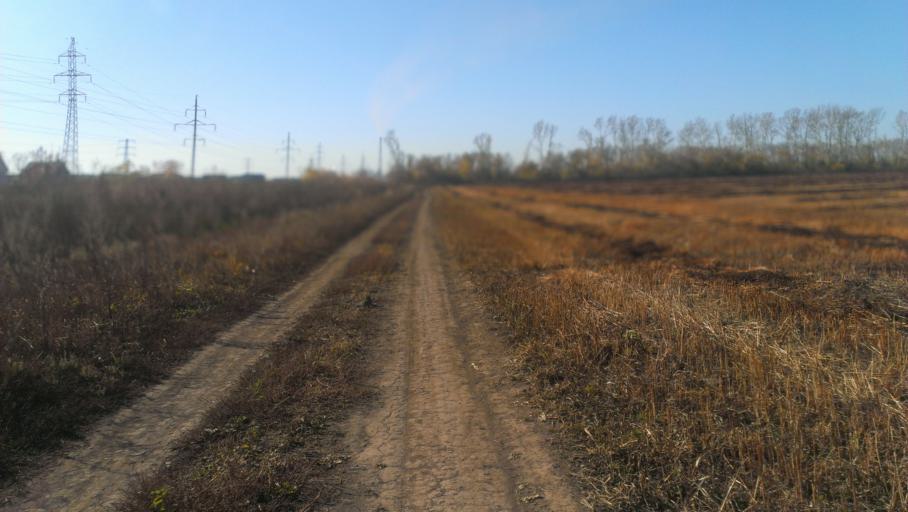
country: RU
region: Altai Krai
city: Novosilikatnyy
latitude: 53.3645
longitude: 83.6396
